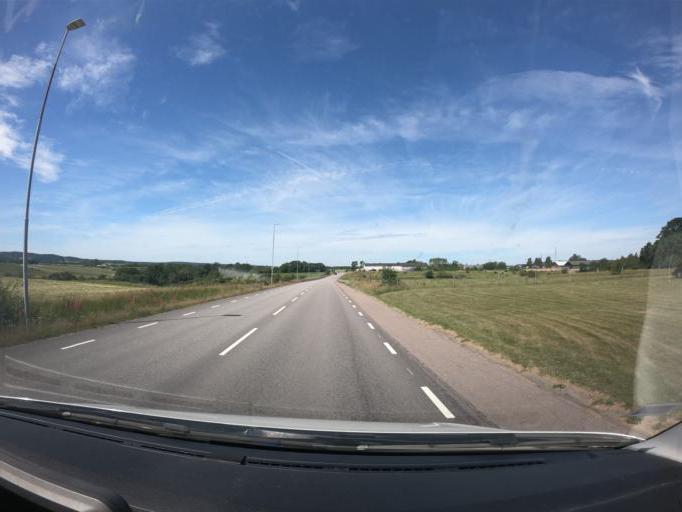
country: SE
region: Skane
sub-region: Klippans Kommun
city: Klippan
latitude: 56.1286
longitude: 13.1194
